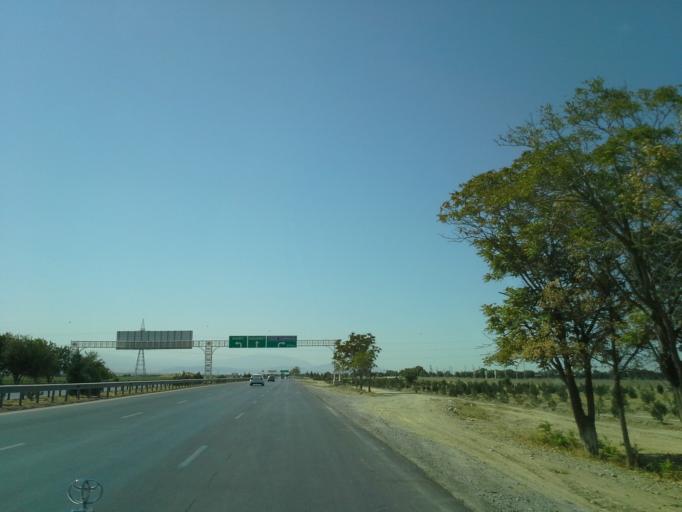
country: TM
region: Ahal
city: Annau
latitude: 37.9037
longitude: 58.5510
